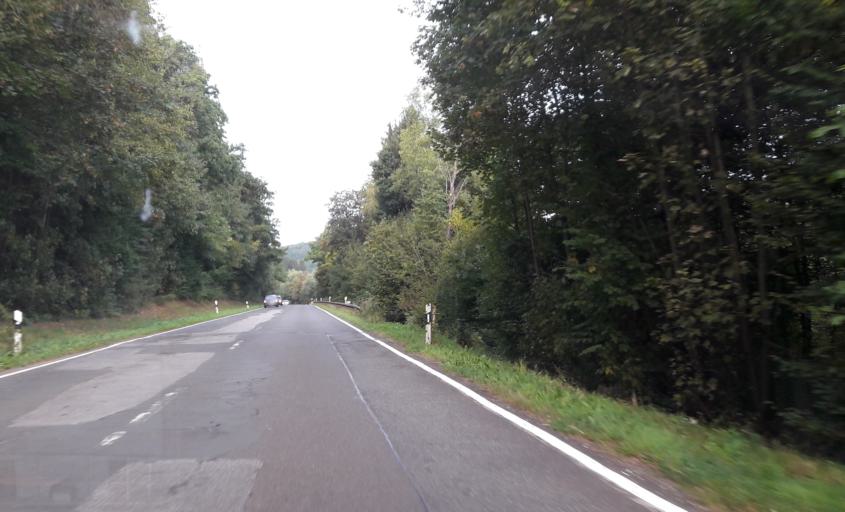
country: DE
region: Rheinland-Pfalz
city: Ellweiler
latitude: 49.6095
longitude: 7.1727
